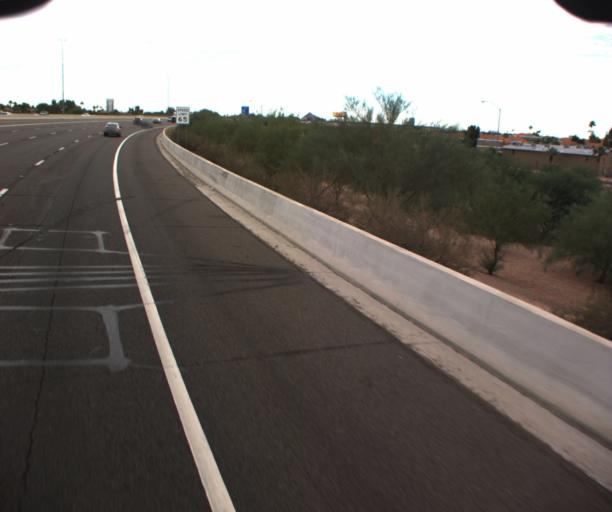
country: US
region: Arizona
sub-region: Maricopa County
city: Tempe Junction
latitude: 33.4555
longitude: -111.9734
